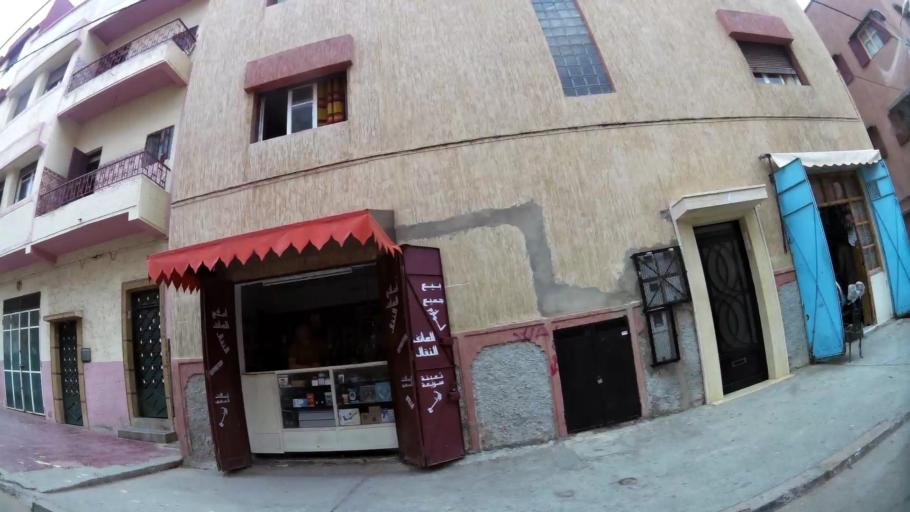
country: MA
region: Rabat-Sale-Zemmour-Zaer
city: Sale
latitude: 34.0415
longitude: -6.8045
